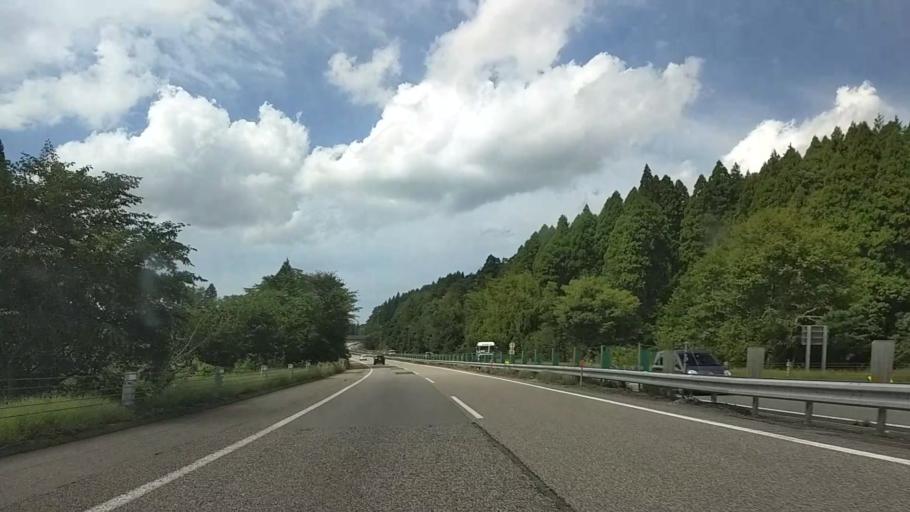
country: JP
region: Ishikawa
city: Tsubata
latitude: 36.6018
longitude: 136.7293
